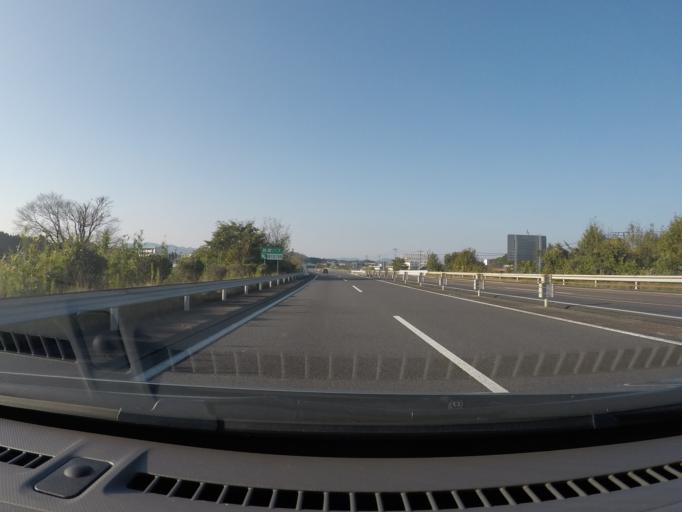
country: JP
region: Kagoshima
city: Kajiki
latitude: 31.7985
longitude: 130.7140
